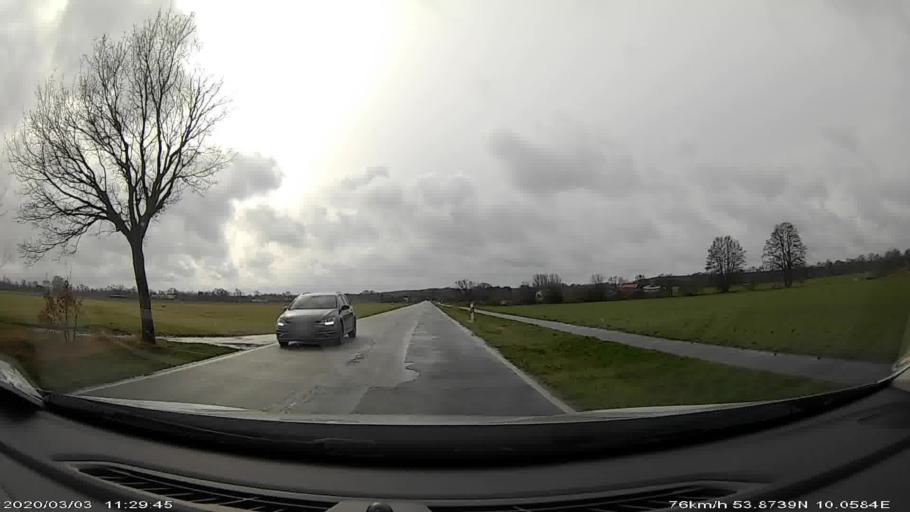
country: DE
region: Schleswig-Holstein
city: Struvenhutten
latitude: 53.8711
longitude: 10.0574
